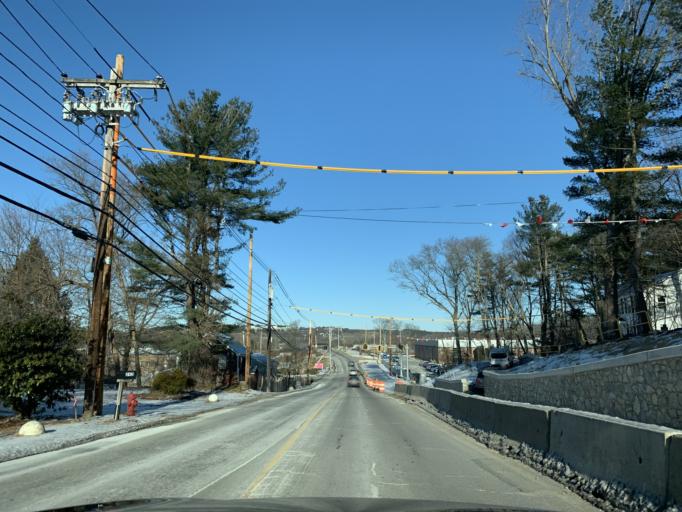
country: US
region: Massachusetts
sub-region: Norfolk County
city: Canton
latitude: 42.1897
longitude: -71.1494
